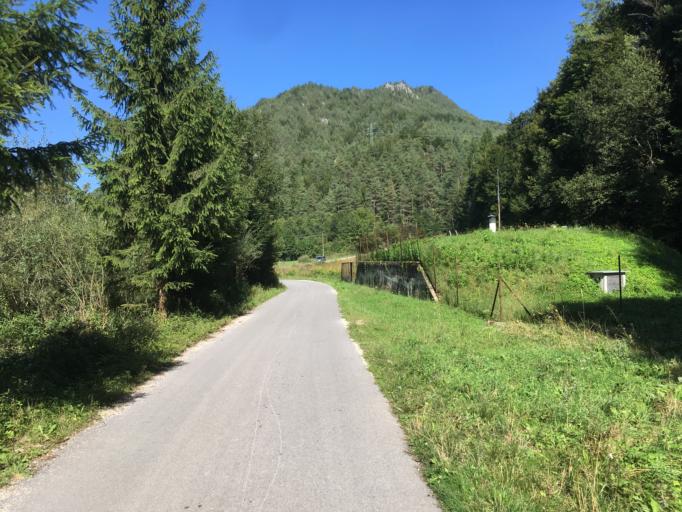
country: SK
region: Trenciansky
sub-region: Okres Povazska Bystrica
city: Povazska Bystrica
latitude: 49.0161
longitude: 18.4405
